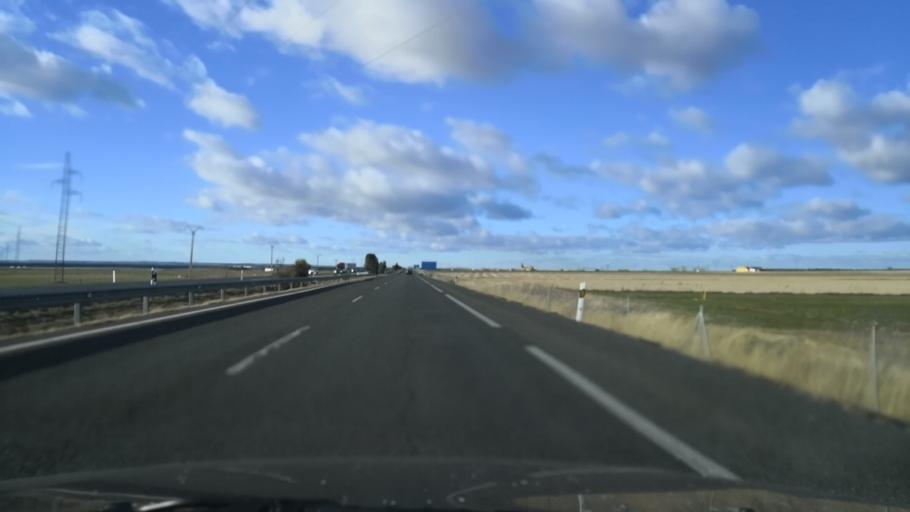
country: ES
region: Castille and Leon
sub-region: Provincia de Avila
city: Gutierre-Munoz
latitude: 40.9681
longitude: -4.6267
